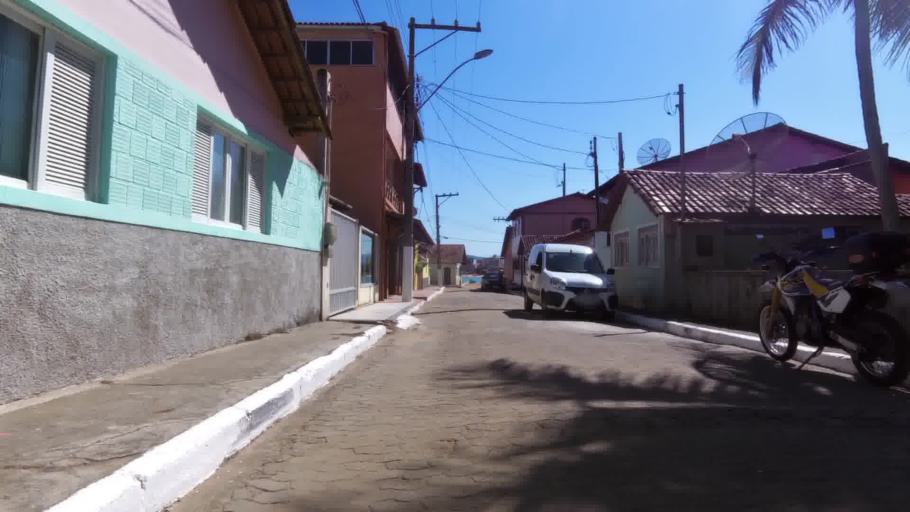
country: BR
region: Espirito Santo
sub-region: Guarapari
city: Guarapari
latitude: -20.7418
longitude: -40.5357
